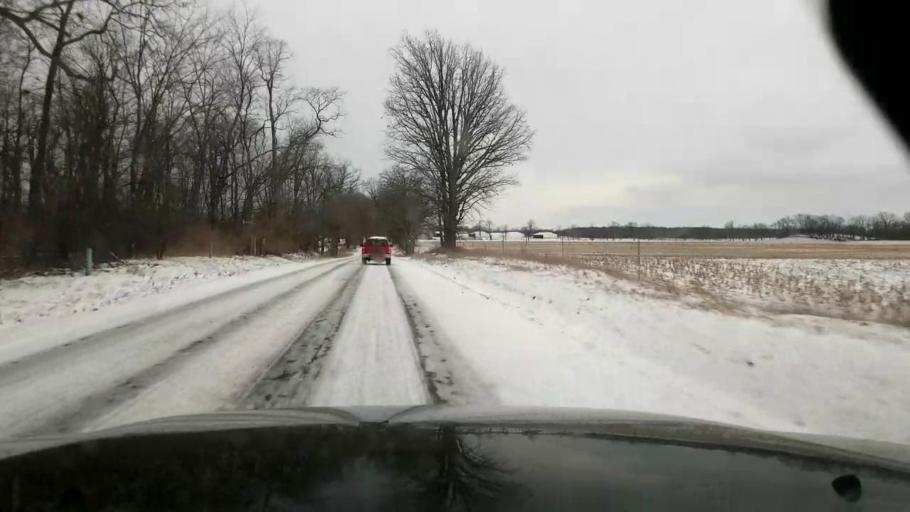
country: US
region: Michigan
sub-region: Jackson County
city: Spring Arbor
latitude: 42.1740
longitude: -84.5006
